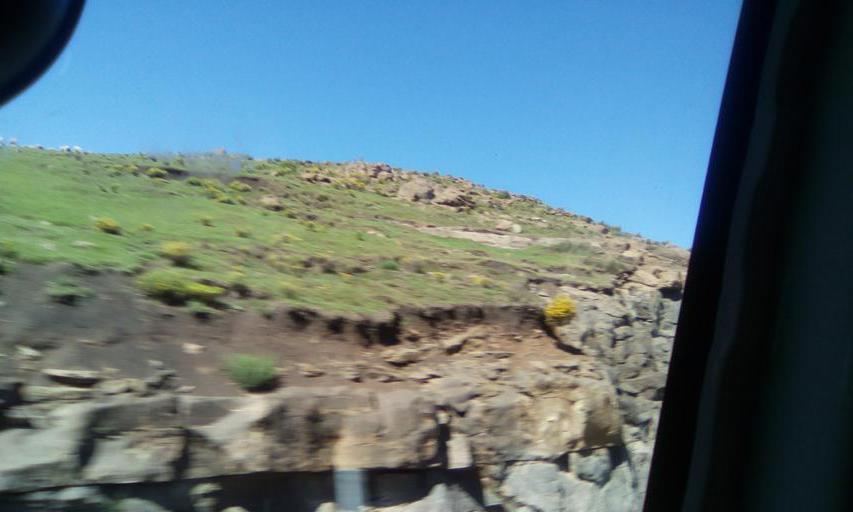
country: LS
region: Maseru
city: Nako
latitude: -29.8917
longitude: 28.1236
